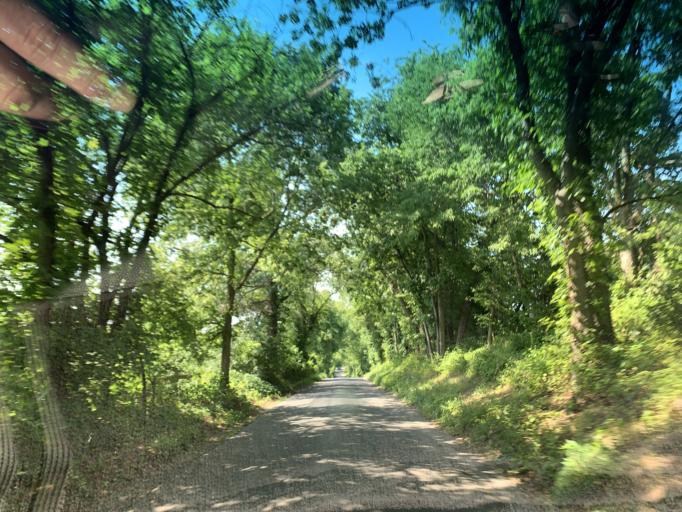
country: US
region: Maryland
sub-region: Montgomery County
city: Poolesville
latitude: 39.1347
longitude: -77.4489
